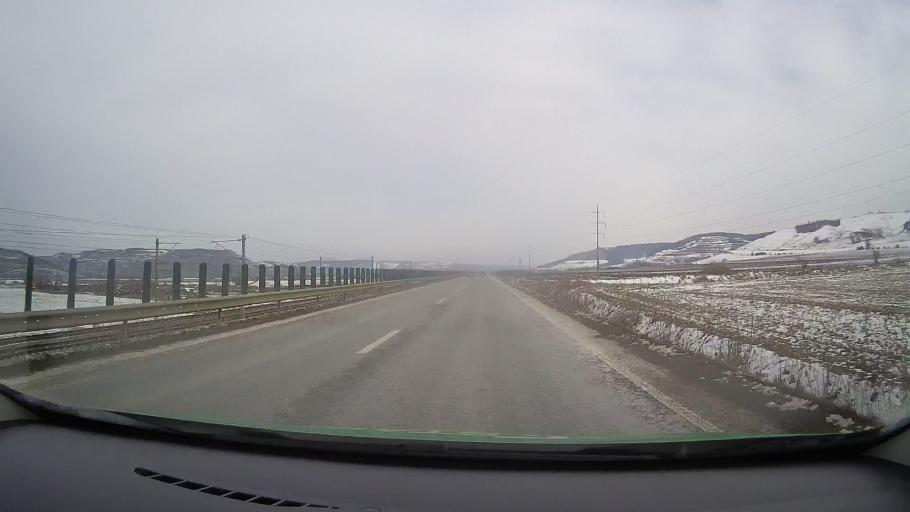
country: RO
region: Sibiu
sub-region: Comuna Brateiu
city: Brateiu
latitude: 46.1862
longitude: 24.4493
